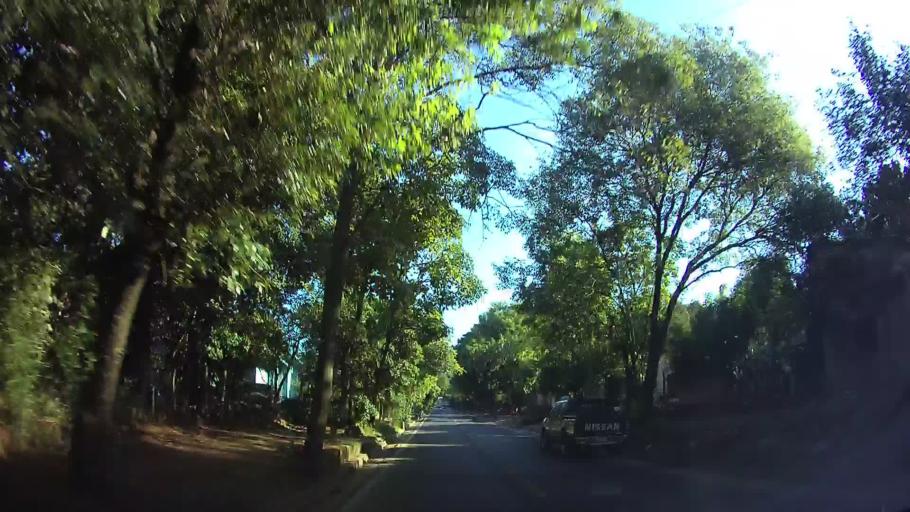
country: PY
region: Central
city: Aregua
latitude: -25.3152
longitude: -57.3811
